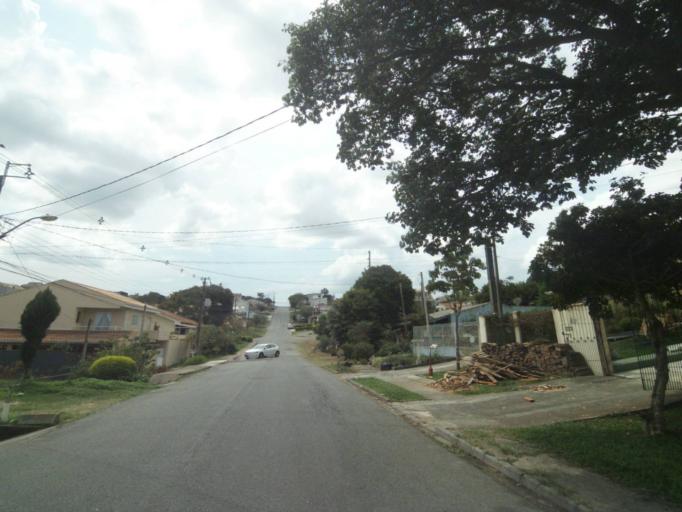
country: BR
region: Parana
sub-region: Pinhais
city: Pinhais
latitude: -25.4016
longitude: -49.1959
